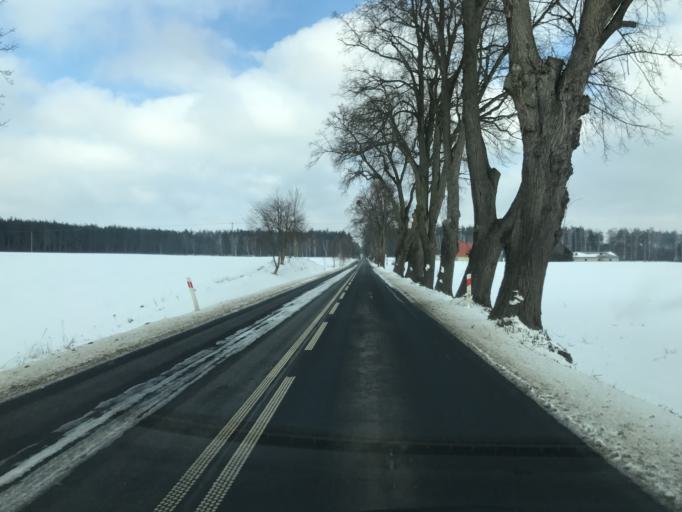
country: PL
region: Warmian-Masurian Voivodeship
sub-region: Powiat dzialdowski
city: Lidzbark
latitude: 53.2902
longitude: 19.8153
